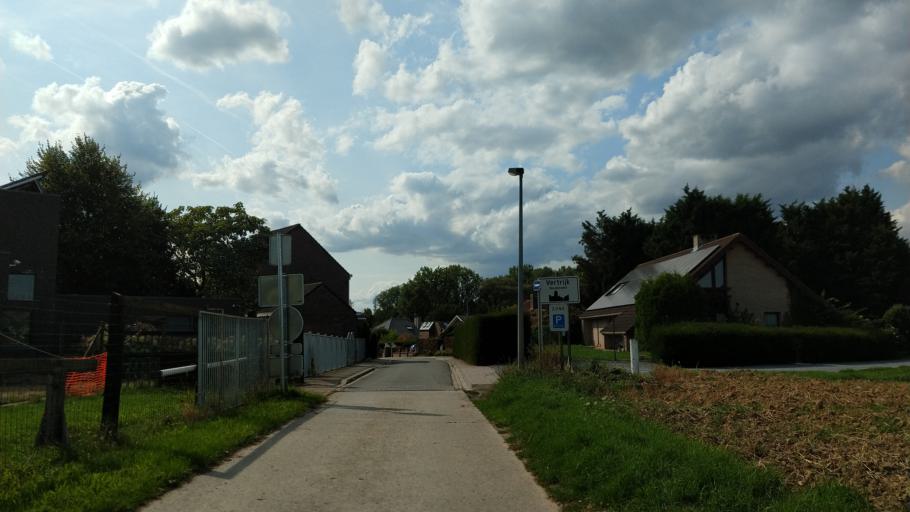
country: BE
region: Flanders
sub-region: Provincie Vlaams-Brabant
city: Boutersem
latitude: 50.8315
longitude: 4.8399
